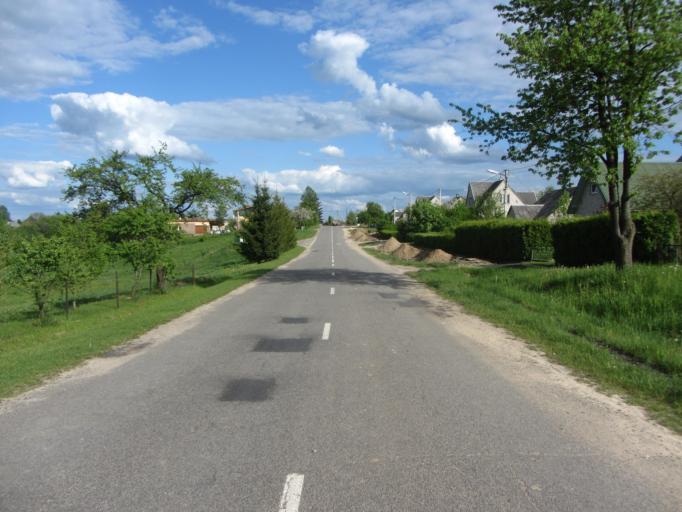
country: LT
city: Sirvintos
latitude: 55.0526
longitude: 24.9352
